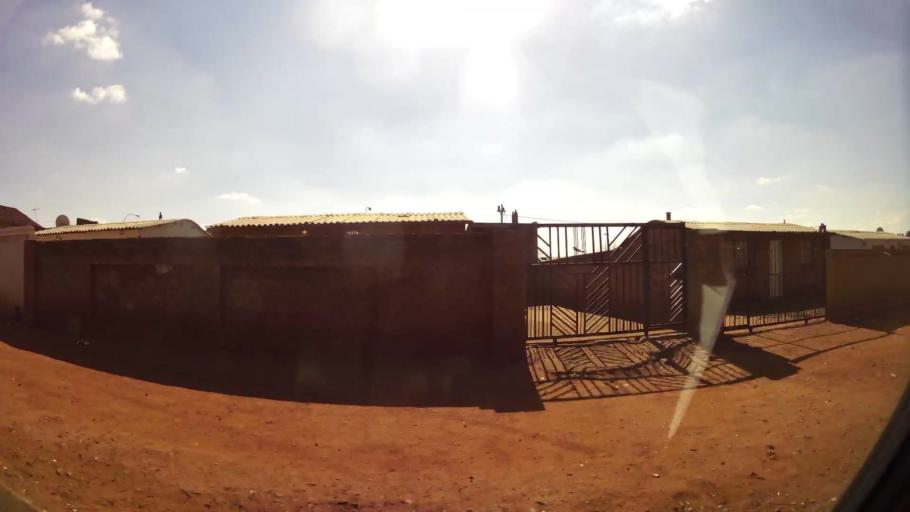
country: ZA
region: Gauteng
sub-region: City of Johannesburg Metropolitan Municipality
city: Soweto
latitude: -26.2403
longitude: 27.8868
